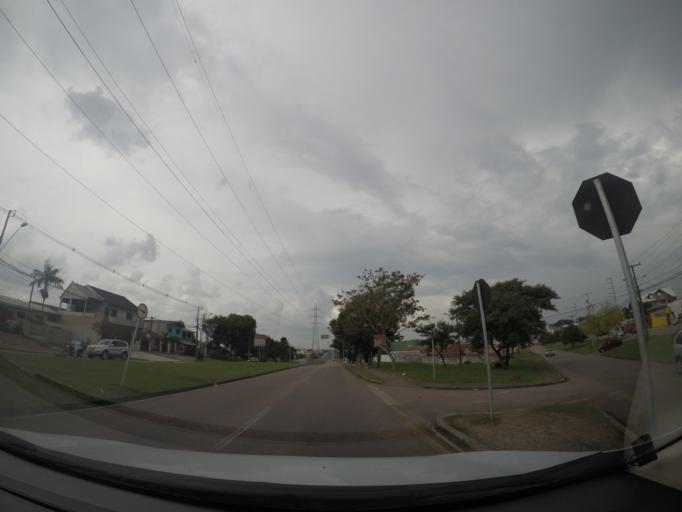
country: BR
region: Parana
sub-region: Sao Jose Dos Pinhais
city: Sao Jose dos Pinhais
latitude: -25.5400
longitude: -49.2748
